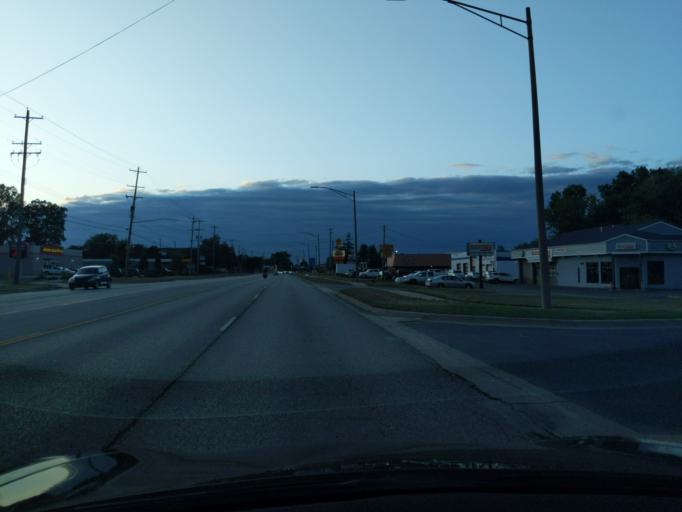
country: US
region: Michigan
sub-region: Ingham County
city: Holt
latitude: 42.6555
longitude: -84.5333
